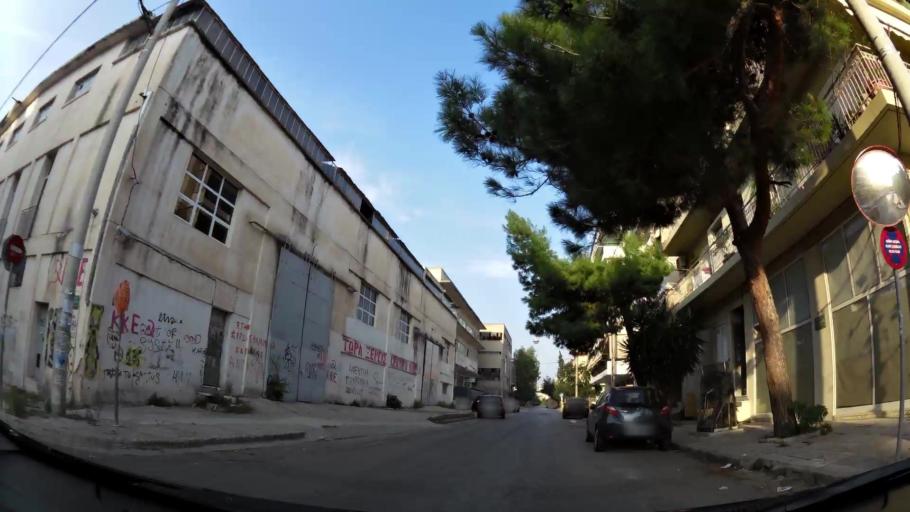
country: GR
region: Attica
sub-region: Nomarchia Athinas
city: Nea Filadelfeia
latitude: 38.0331
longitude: 23.7465
